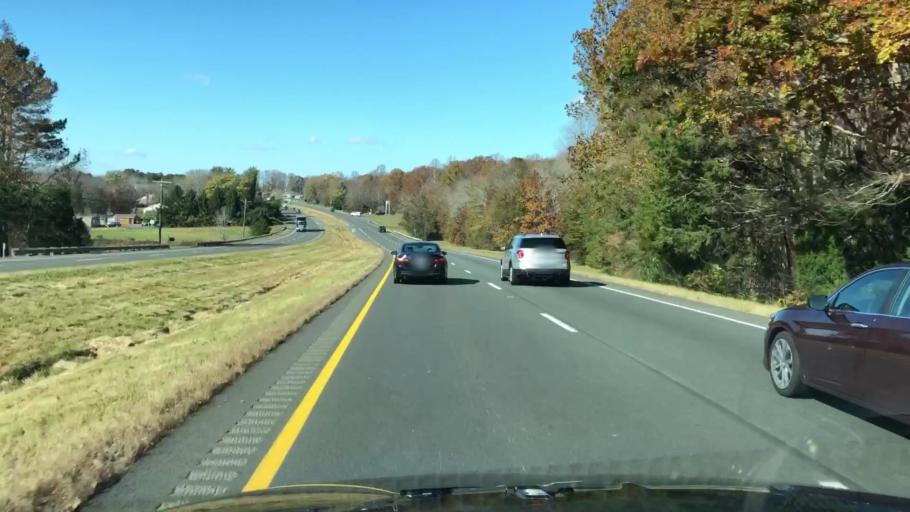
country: US
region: Virginia
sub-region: Fauquier County
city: Bealeton
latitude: 38.4956
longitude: -77.6874
